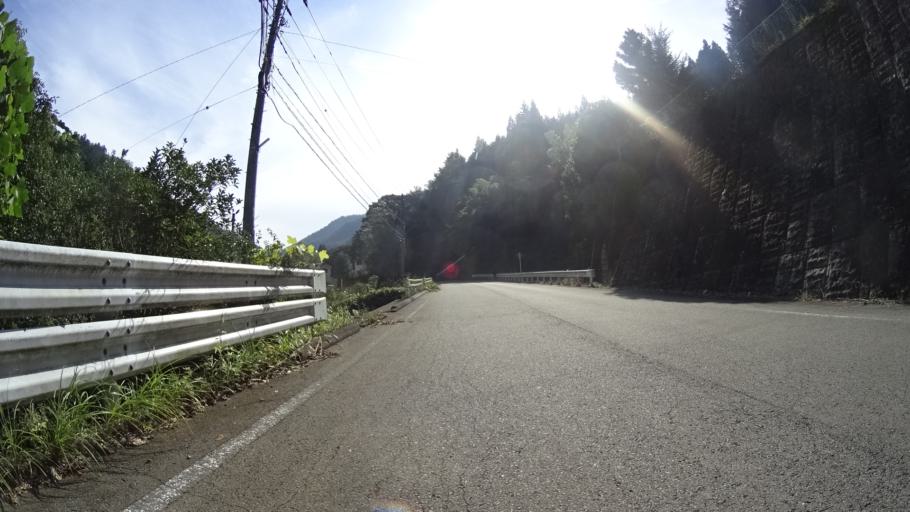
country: JP
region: Yamanashi
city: Otsuki
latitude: 35.5867
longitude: 138.9645
